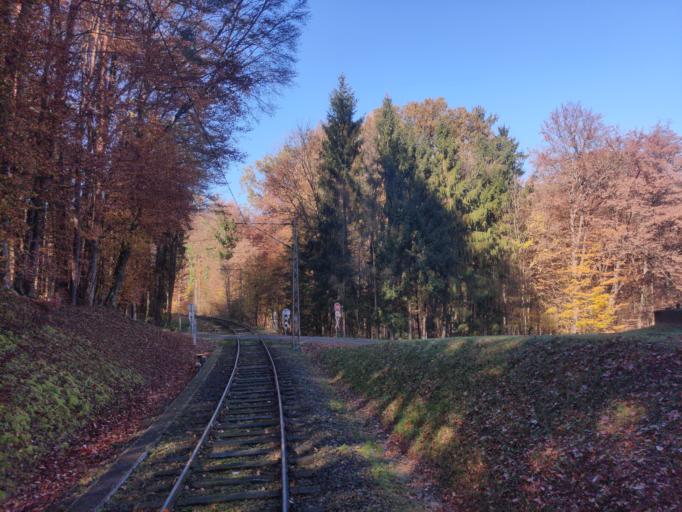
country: AT
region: Styria
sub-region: Politischer Bezirk Suedoststeiermark
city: Trautmannsdorf in Oststeiermark
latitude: 46.8769
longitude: 15.8929
